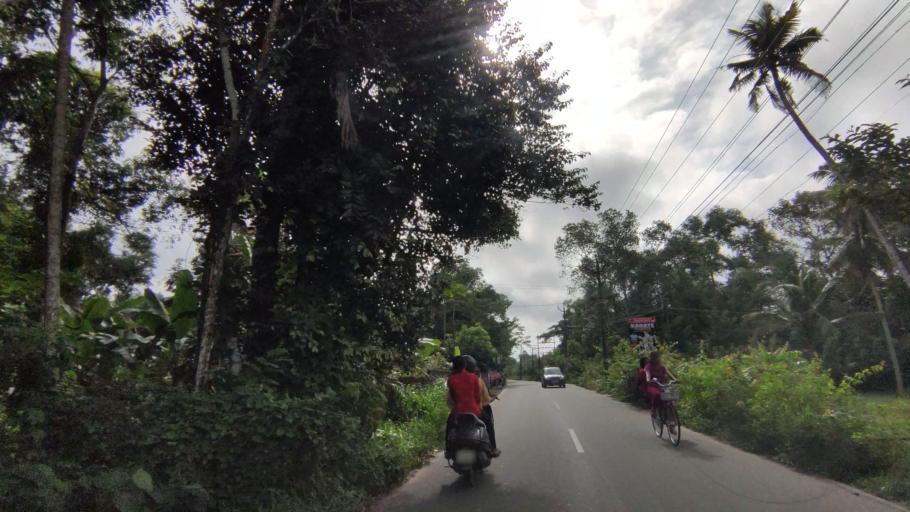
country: IN
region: Kerala
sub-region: Alappuzha
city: Shertallai
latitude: 9.6416
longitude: 76.3581
